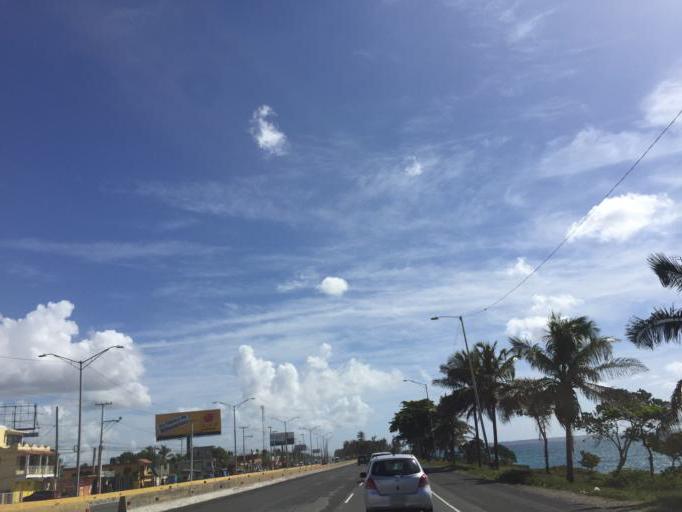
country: DO
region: Santo Domingo
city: Guerra
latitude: 18.4625
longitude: -69.7372
